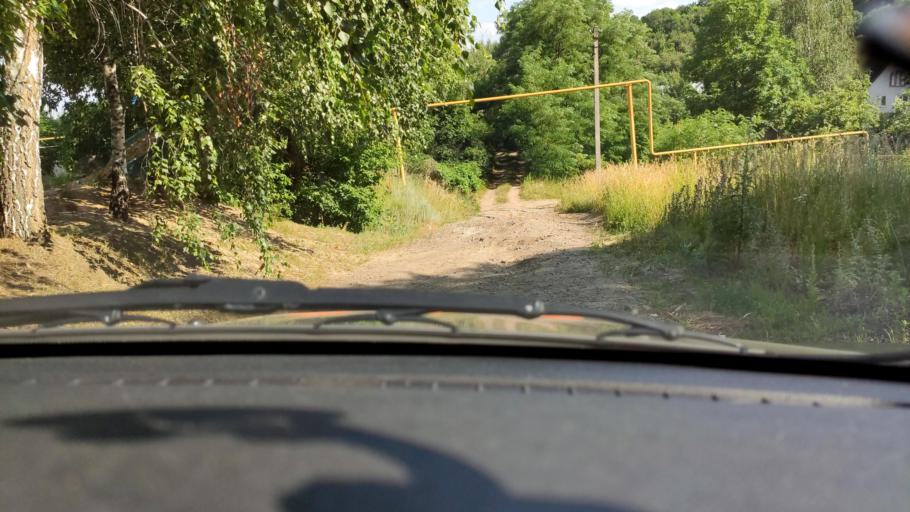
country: RU
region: Voronezj
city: Ramon'
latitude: 51.8229
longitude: 39.2700
